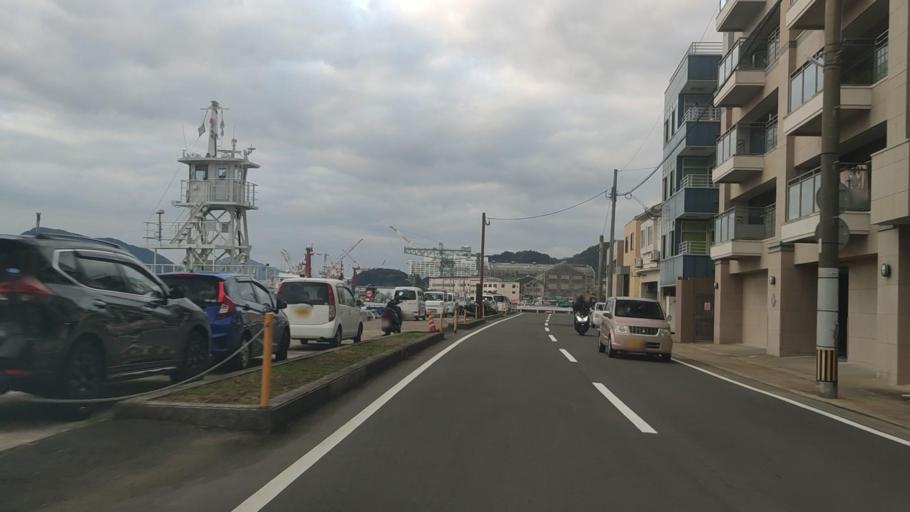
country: JP
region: Nagasaki
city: Nagasaki-shi
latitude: 32.7491
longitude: 129.8651
